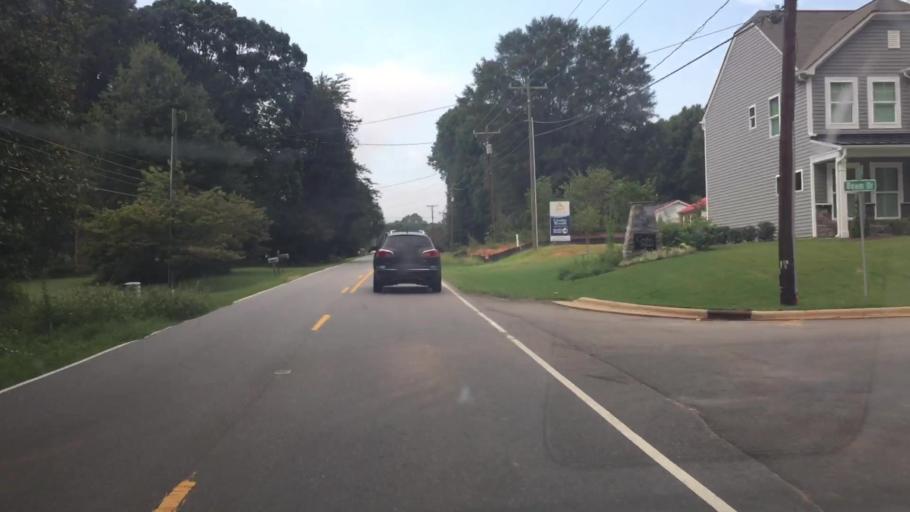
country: US
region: North Carolina
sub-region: Iredell County
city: Mooresville
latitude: 35.6058
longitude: -80.7936
